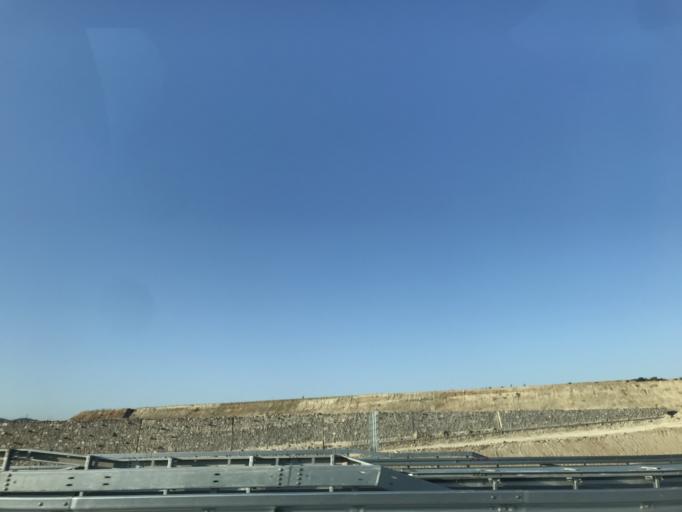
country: TR
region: Bursa
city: Mahmudiye
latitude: 40.2643
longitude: 28.6640
